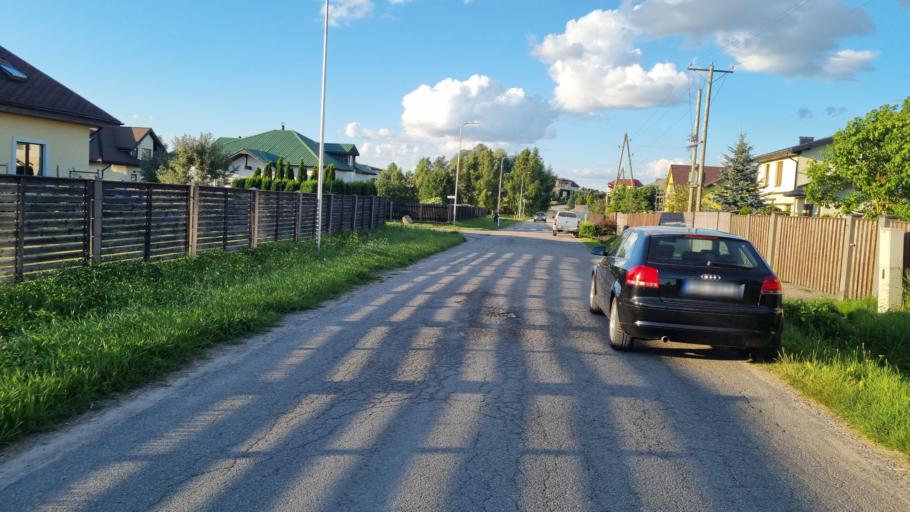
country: LV
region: Kekava
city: Balozi
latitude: 56.8872
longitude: 24.1665
